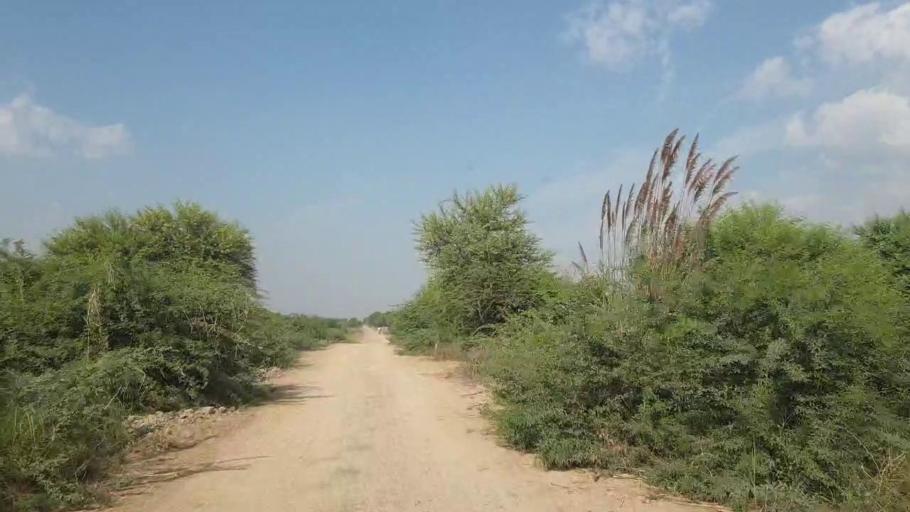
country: PK
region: Sindh
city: Digri
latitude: 25.0228
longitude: 69.0710
